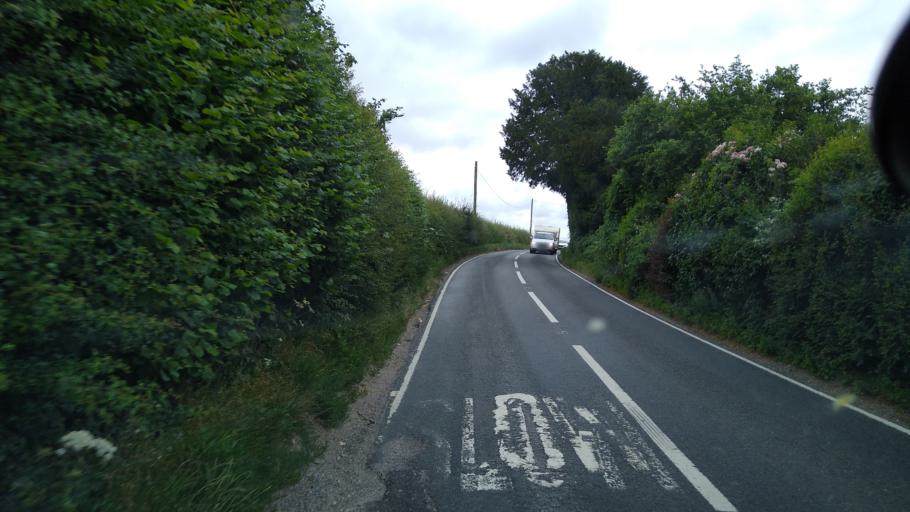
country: GB
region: England
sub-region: Hampshire
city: Alton
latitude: 51.1170
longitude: -0.9477
